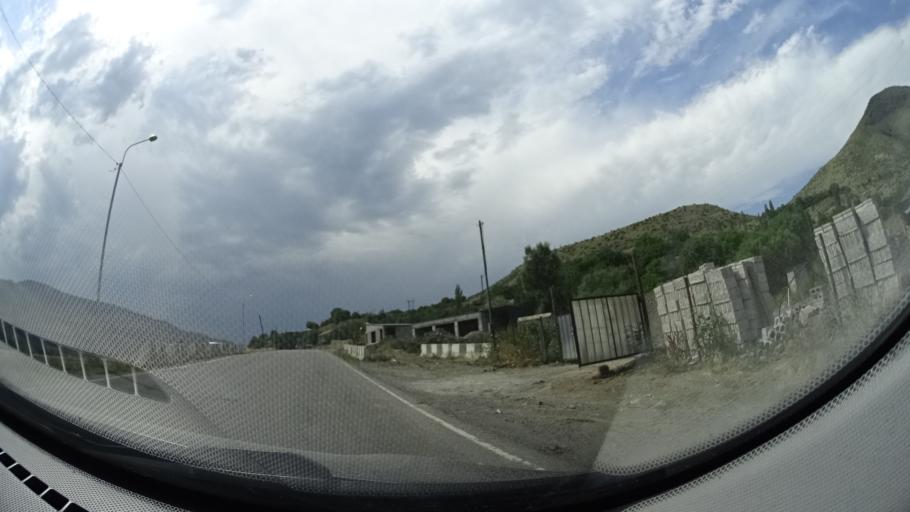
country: GE
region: Samtskhe-Javakheti
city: Aspindza
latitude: 41.5642
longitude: 43.2645
